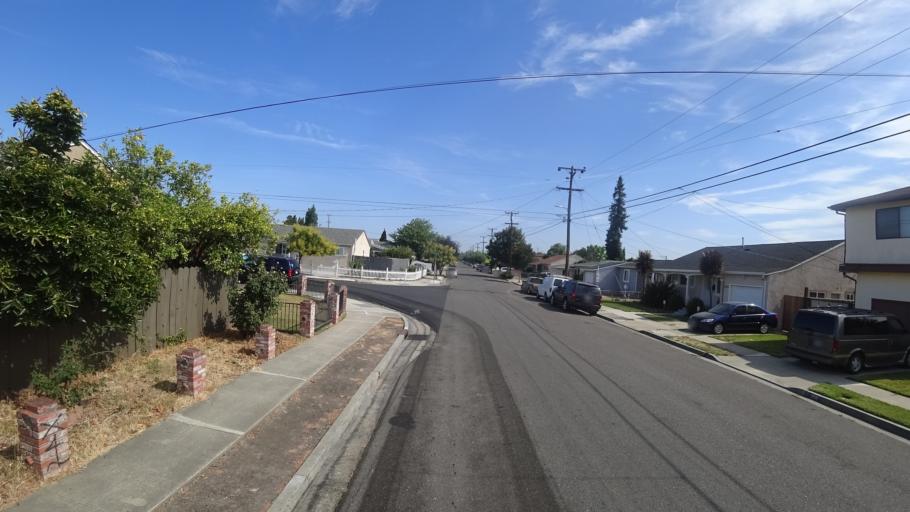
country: US
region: California
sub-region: Alameda County
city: Hayward
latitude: 37.6400
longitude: -122.0852
